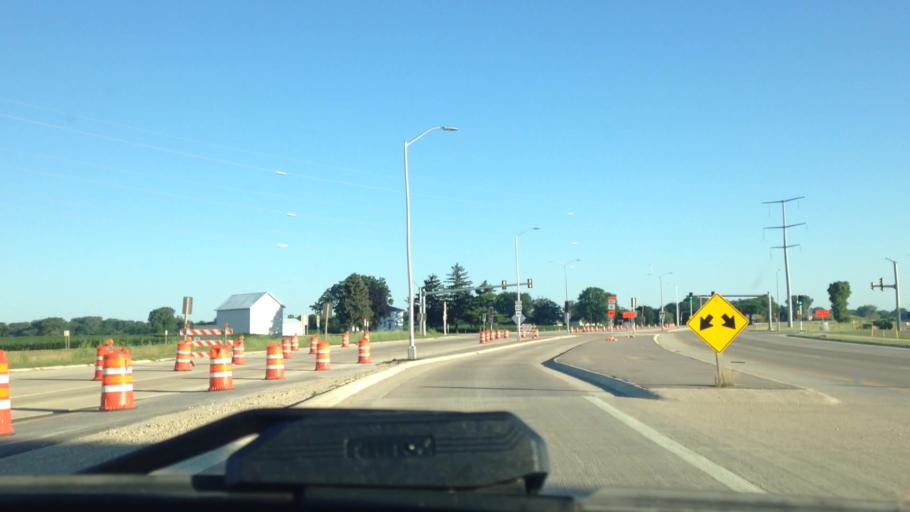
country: US
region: Wisconsin
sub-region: Columbia County
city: Columbus
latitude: 43.3494
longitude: -89.0370
